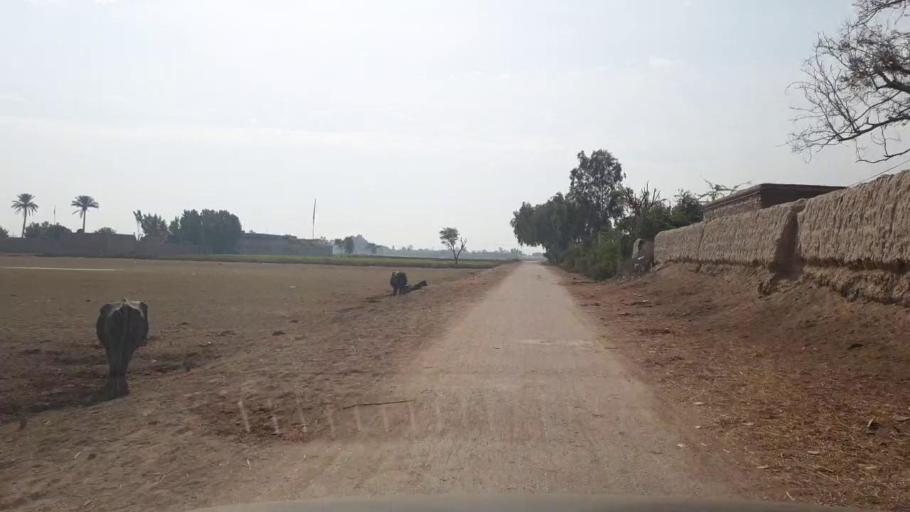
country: PK
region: Sindh
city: Hala
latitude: 25.9937
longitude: 68.4211
